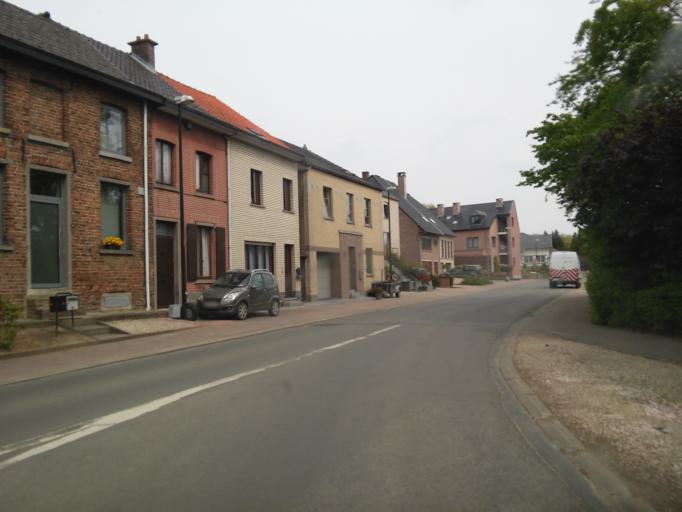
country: BE
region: Flanders
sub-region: Provincie Vlaams-Brabant
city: Sint-Pieters-Leeuw
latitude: 50.7772
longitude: 4.2422
